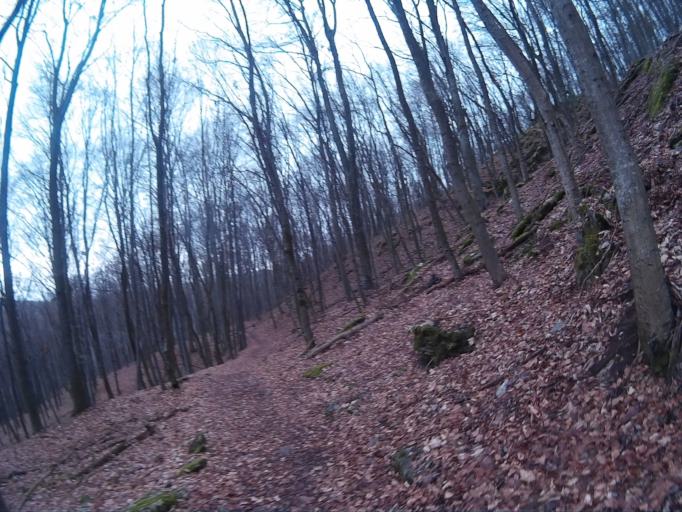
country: HU
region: Heves
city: Belapatfalva
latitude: 48.0574
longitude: 20.4039
